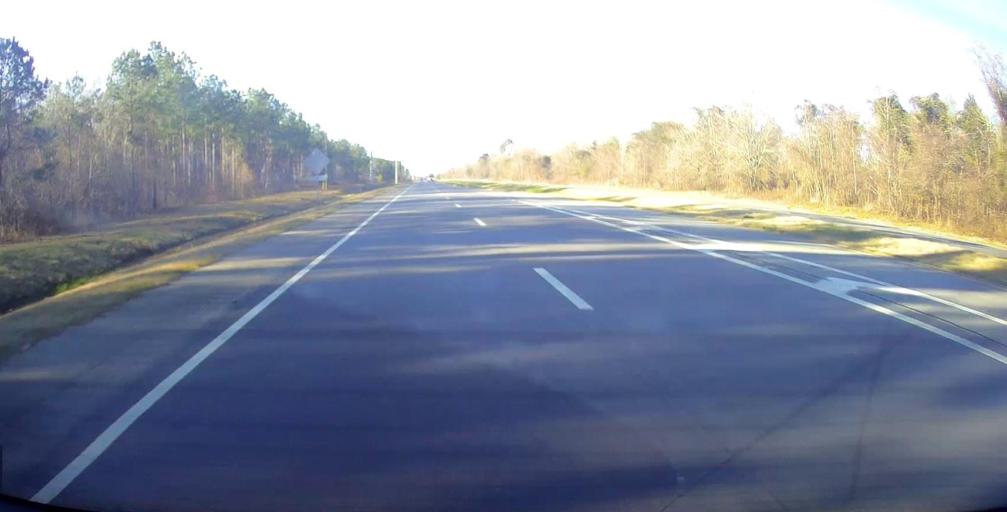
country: US
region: Georgia
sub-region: Lee County
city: Leesburg
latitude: 31.8605
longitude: -84.2331
